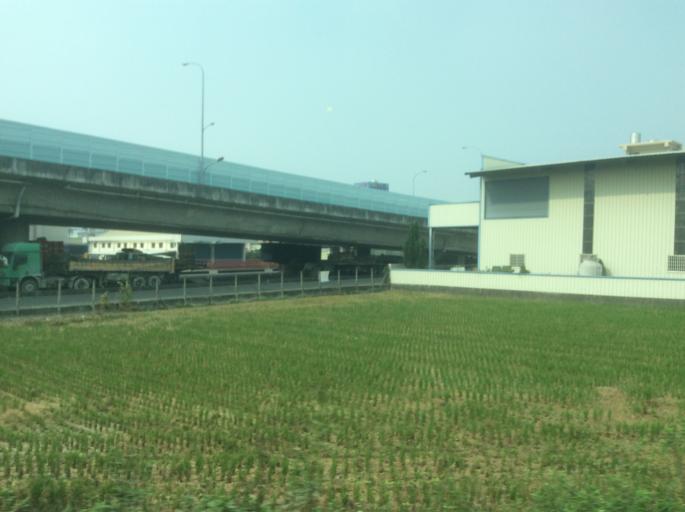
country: TW
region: Taiwan
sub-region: Yunlin
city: Douliu
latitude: 23.7031
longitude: 120.5295
